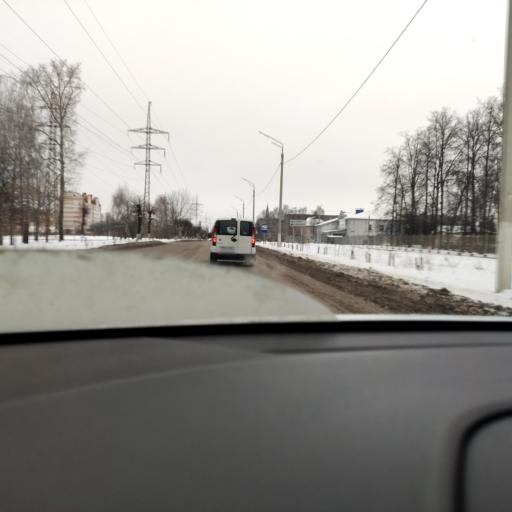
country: RU
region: Tatarstan
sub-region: Zelenodol'skiy Rayon
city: Zelenodolsk
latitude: 55.8537
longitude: 48.4939
